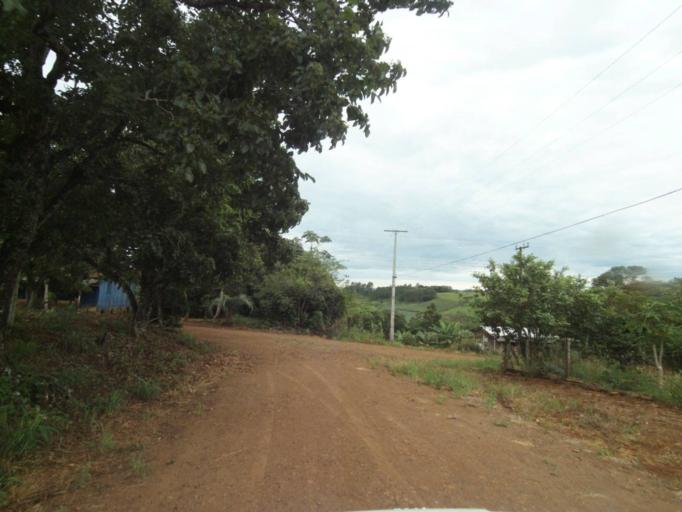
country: BR
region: Parana
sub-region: Guaraniacu
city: Guaraniacu
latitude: -24.9177
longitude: -52.9362
